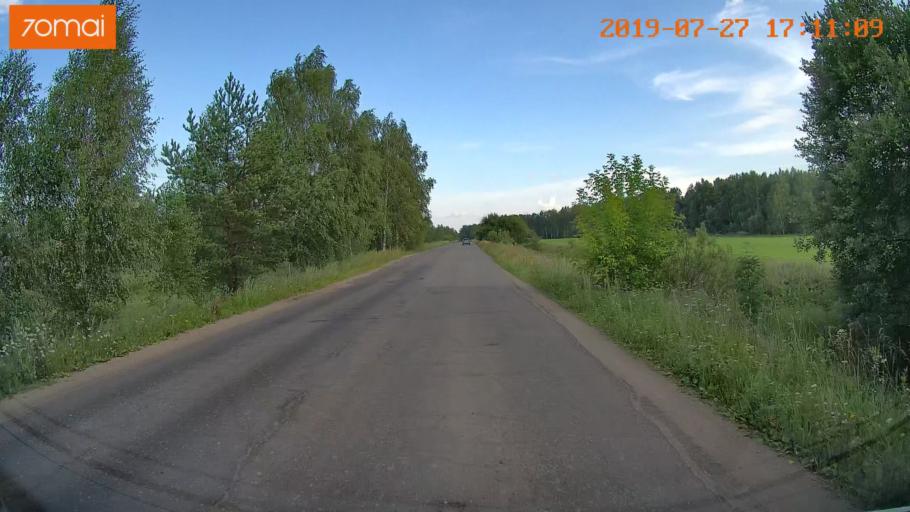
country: RU
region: Ivanovo
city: Novo-Talitsy
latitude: 57.0665
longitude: 40.8581
